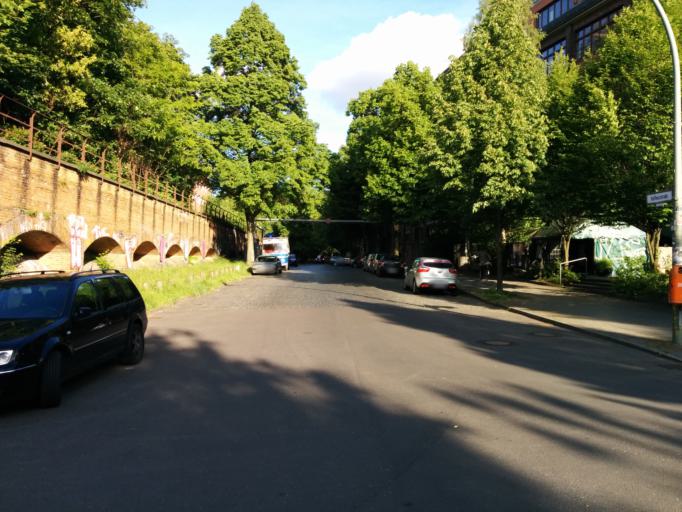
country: DE
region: Berlin
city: Berlin Treptow
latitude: 52.4935
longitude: 13.4454
